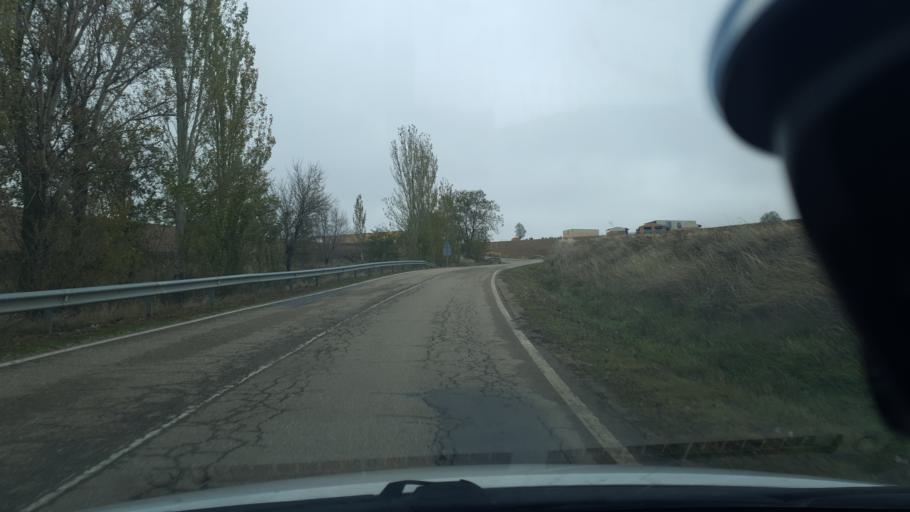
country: ES
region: Castille and Leon
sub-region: Provincia de Segovia
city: Valseca
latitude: 41.0033
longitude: -4.1650
